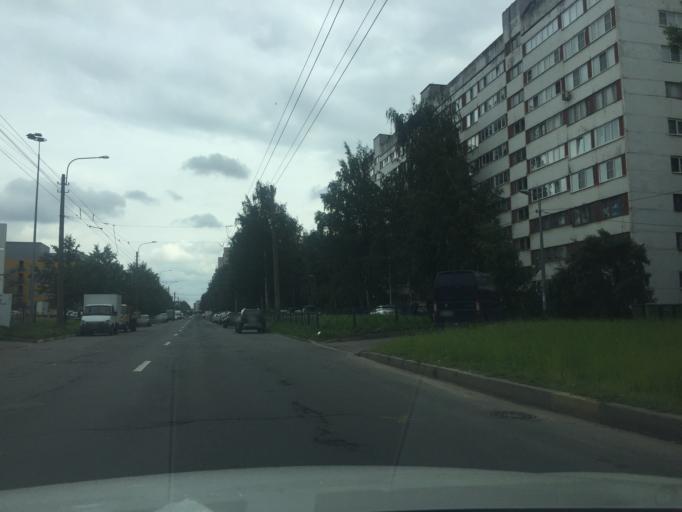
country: RU
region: Leningrad
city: Parnas
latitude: 60.0576
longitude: 30.3503
